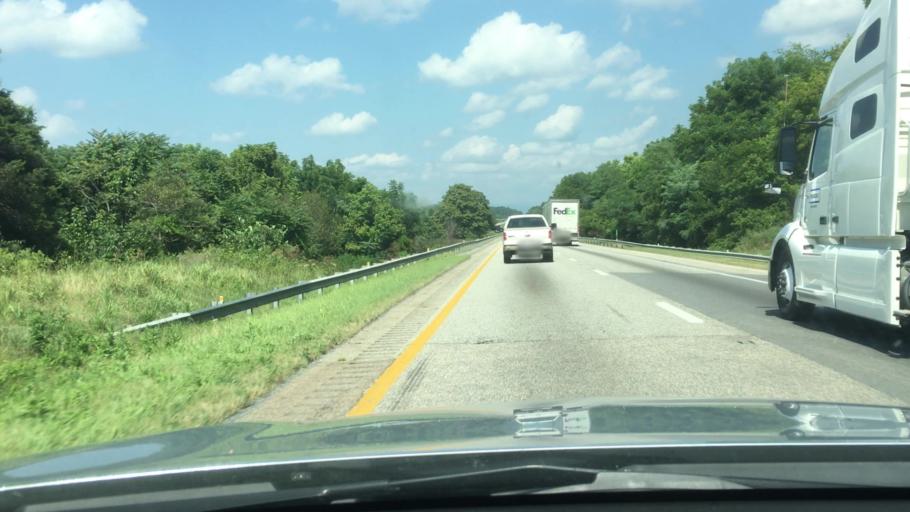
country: US
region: Virginia
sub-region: Rockbridge County
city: Glasgow
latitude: 37.6550
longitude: -79.5419
